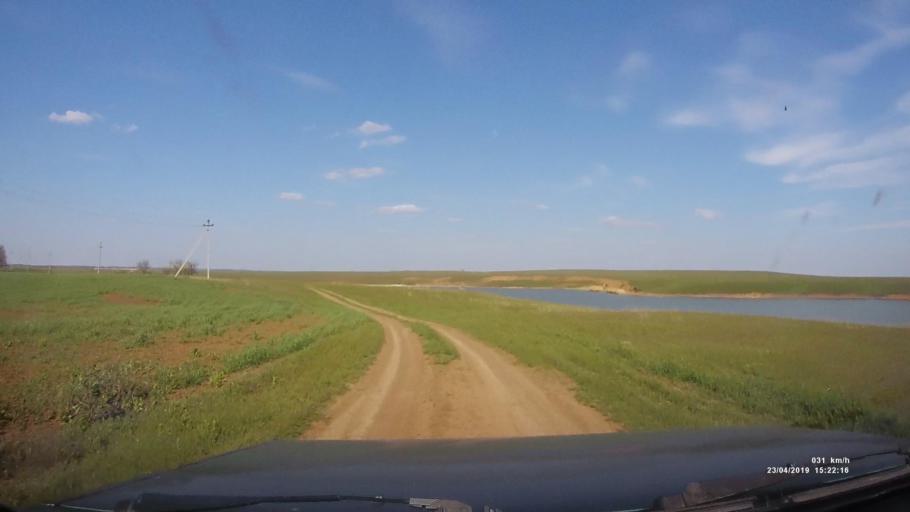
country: RU
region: Rostov
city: Remontnoye
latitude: 46.5279
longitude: 42.9693
